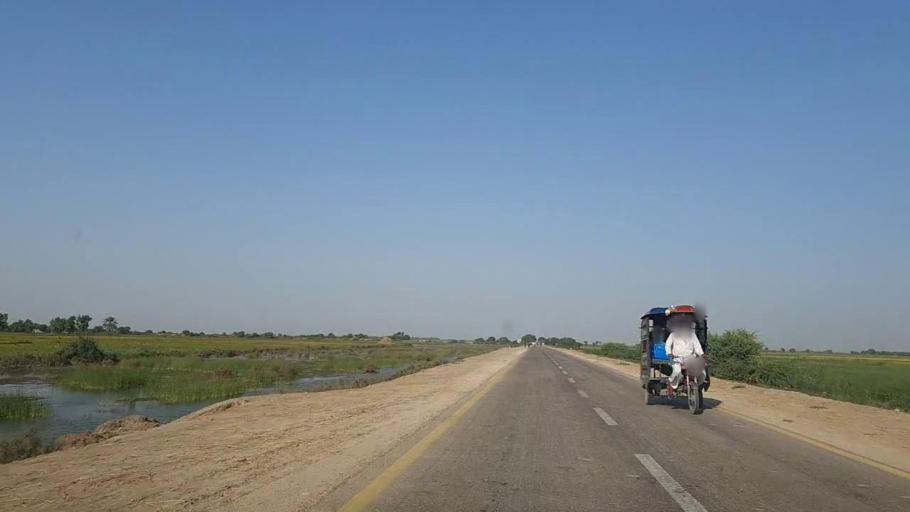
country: PK
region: Sindh
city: Jati
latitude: 24.4098
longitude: 68.2992
